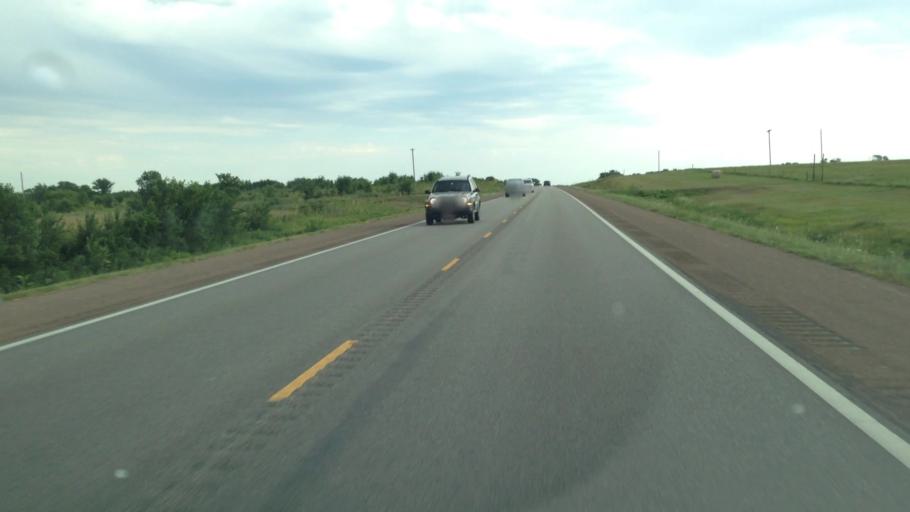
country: US
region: Kansas
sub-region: Woodson County
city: Yates Center
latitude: 38.0117
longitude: -95.7392
